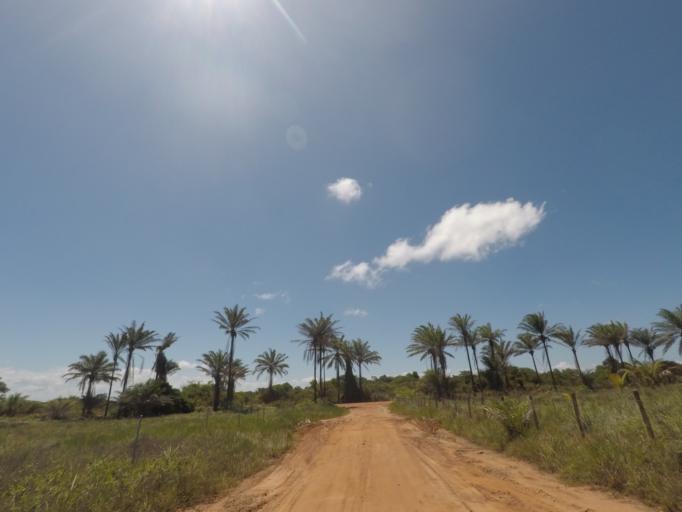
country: BR
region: Bahia
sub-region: Marau
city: Marau
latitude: -13.9671
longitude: -38.9470
